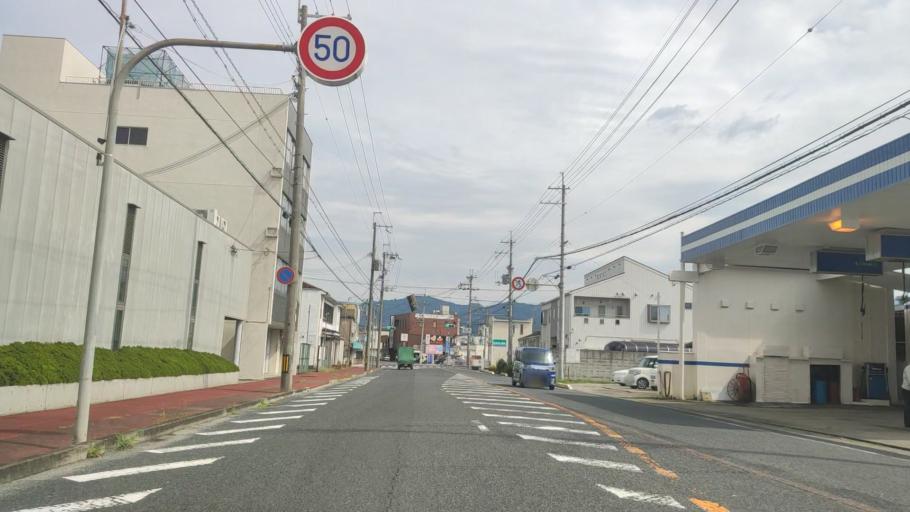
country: JP
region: Wakayama
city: Hashimoto
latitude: 34.3028
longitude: 135.5544
